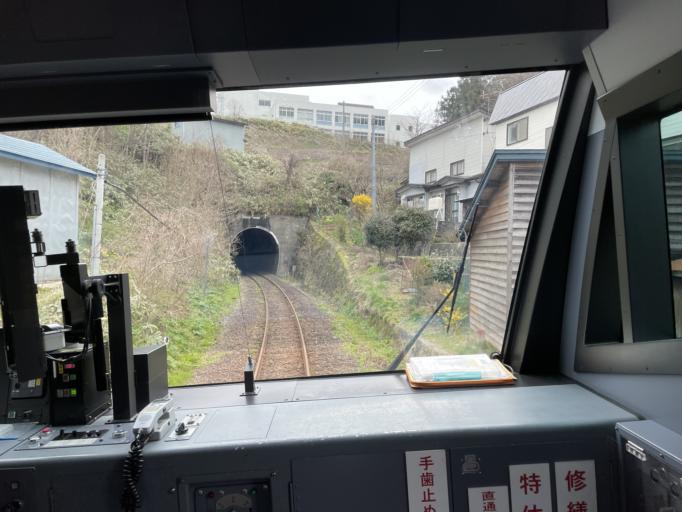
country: JP
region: Akita
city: Noshiromachi
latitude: 40.6397
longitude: 139.9259
